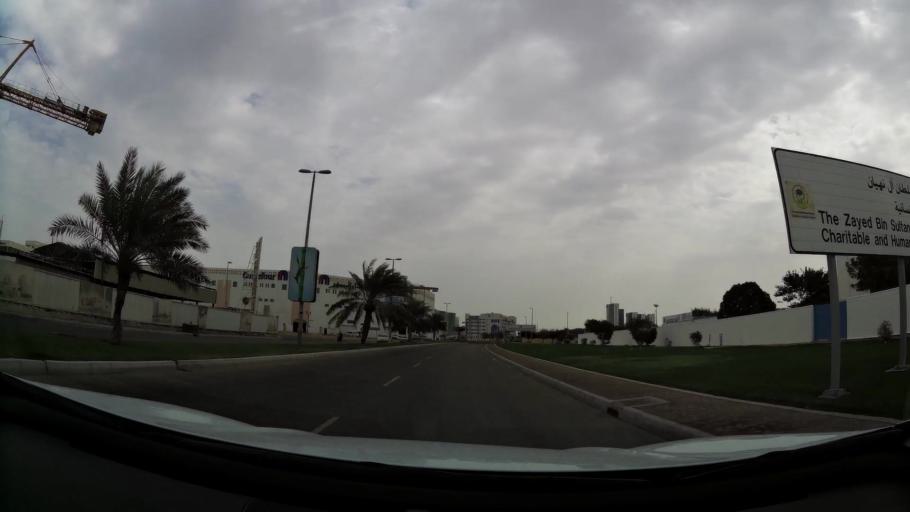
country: AE
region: Abu Dhabi
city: Abu Dhabi
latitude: 24.4231
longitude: 54.4498
